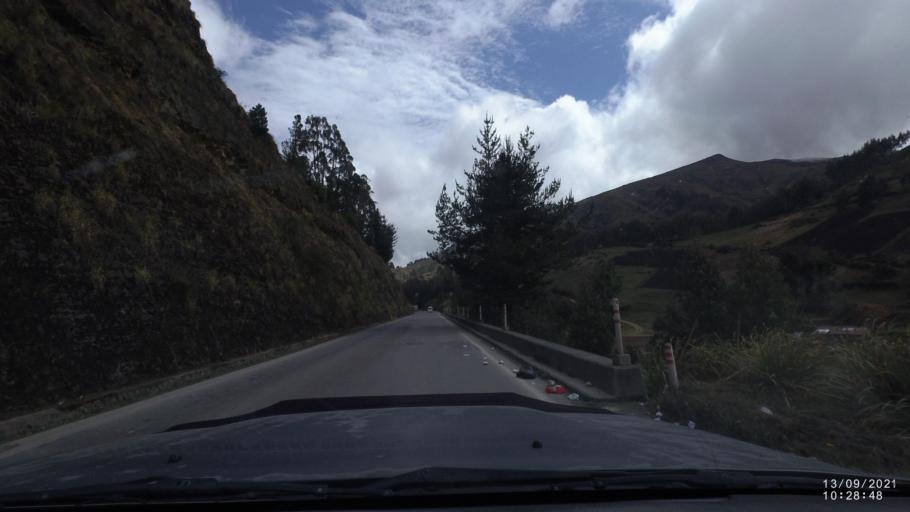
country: BO
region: Cochabamba
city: Colomi
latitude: -17.2755
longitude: -65.8754
